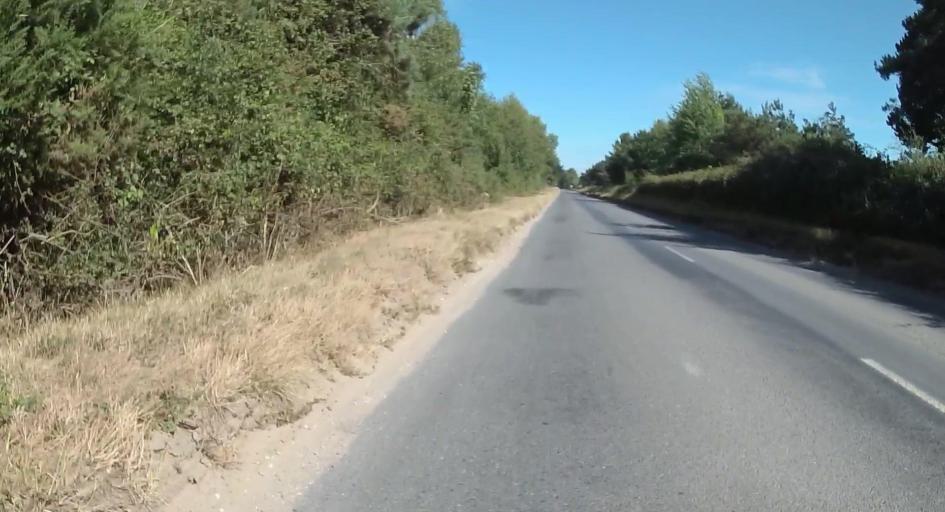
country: GB
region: England
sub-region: Dorset
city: Wool
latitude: 50.6962
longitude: -2.1841
